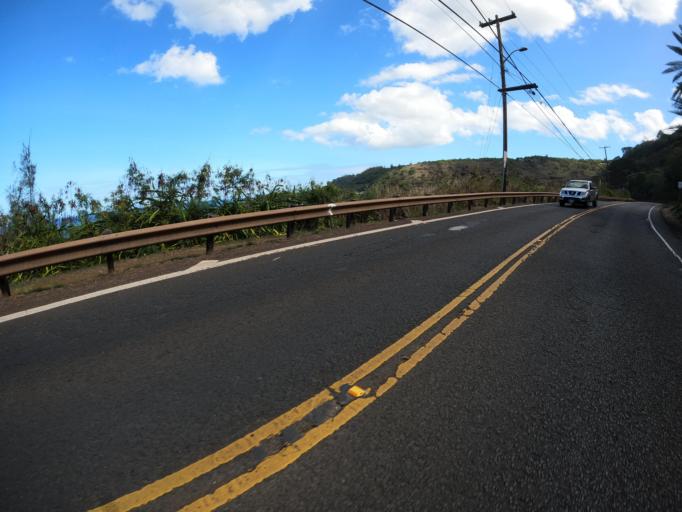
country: US
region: Hawaii
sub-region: Honolulu County
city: Pupukea
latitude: 21.6376
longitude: -158.0653
